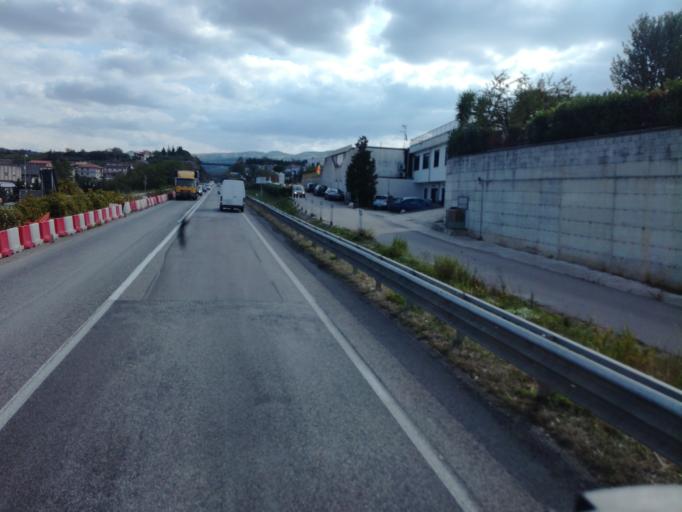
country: IT
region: Campania
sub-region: Provincia di Benevento
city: Ponte
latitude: 41.2079
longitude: 14.6923
